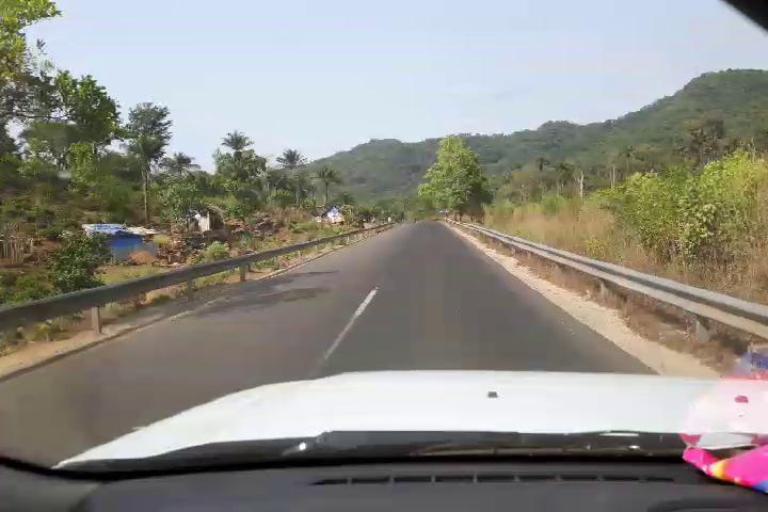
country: SL
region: Western Area
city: Waterloo
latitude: 8.2713
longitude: -13.1586
